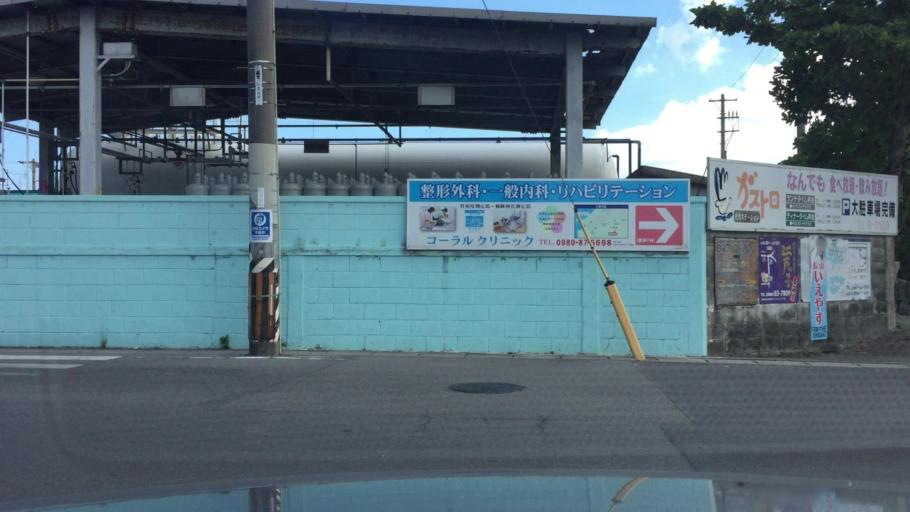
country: JP
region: Okinawa
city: Ishigaki
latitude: 24.3395
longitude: 124.1541
